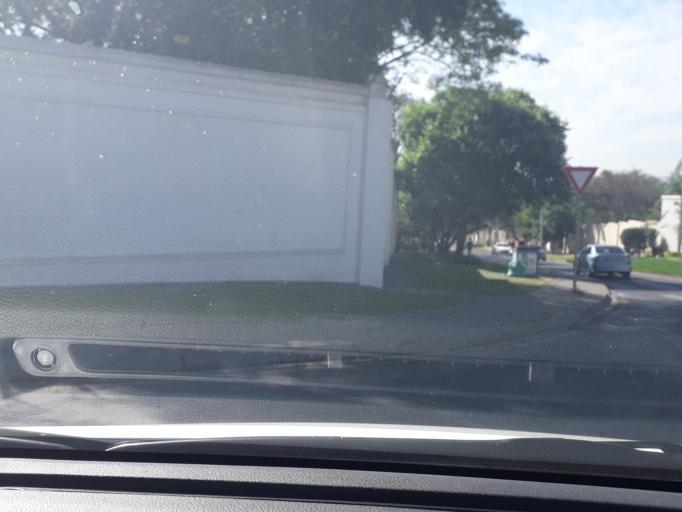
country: ZA
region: Gauteng
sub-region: City of Johannesburg Metropolitan Municipality
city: Midrand
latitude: -26.0625
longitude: 28.0274
